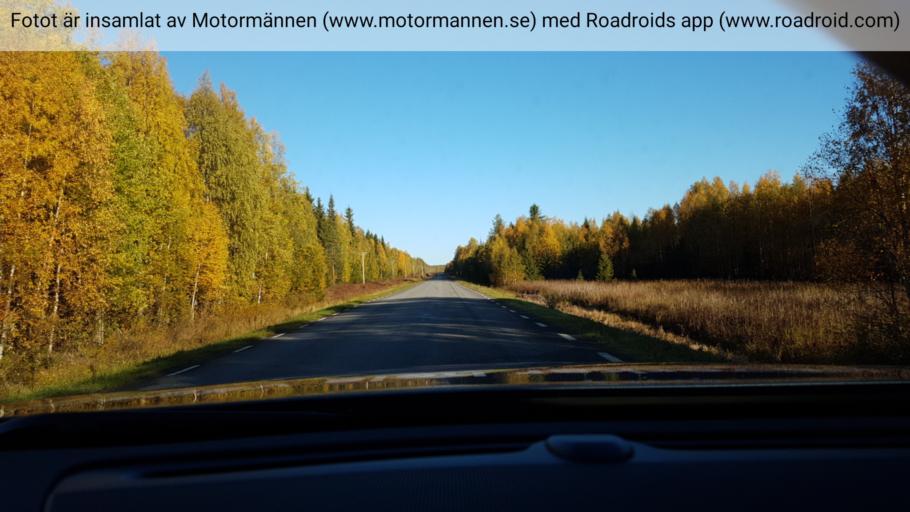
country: SE
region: Norrbotten
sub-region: Bodens Kommun
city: Boden
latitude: 65.9063
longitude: 21.6670
